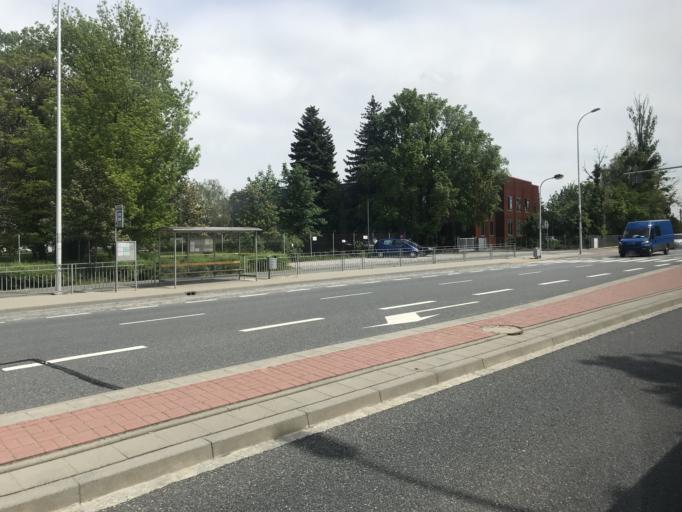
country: PL
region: Lower Silesian Voivodeship
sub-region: Powiat wroclawski
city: Smolec
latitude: 51.1085
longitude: 16.9090
